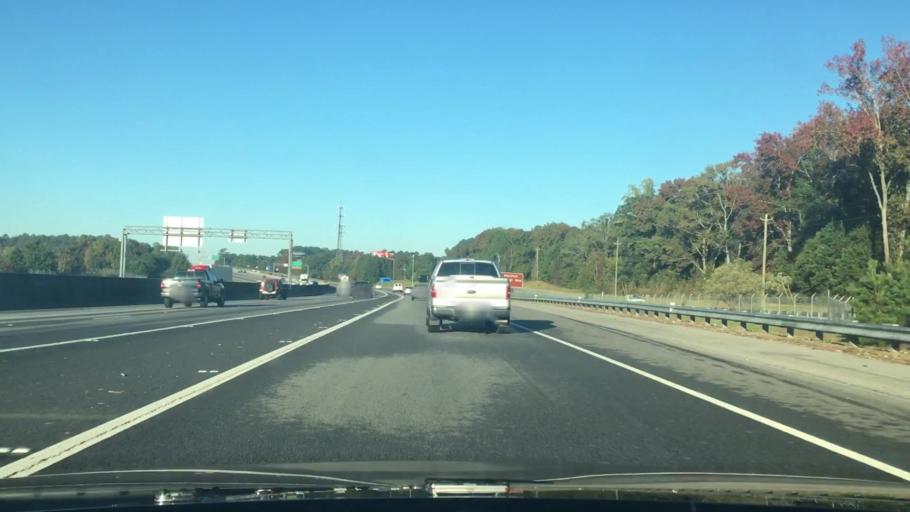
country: US
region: Georgia
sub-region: DeKalb County
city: Lithonia
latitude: 33.7024
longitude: -84.0972
